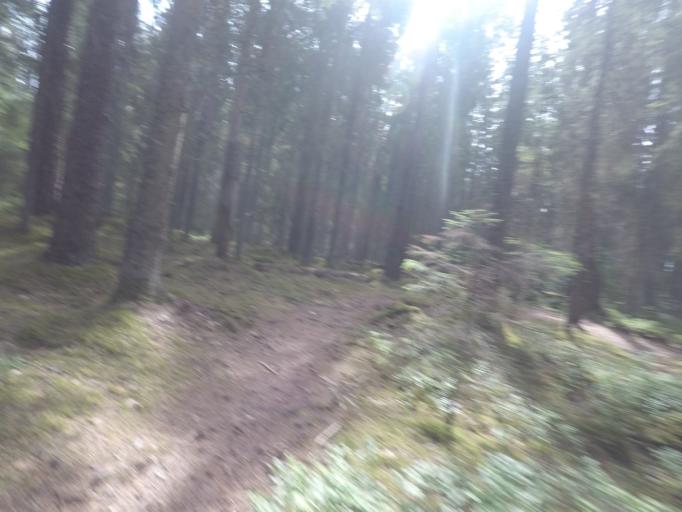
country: SE
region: Vaestmanland
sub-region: Kungsors Kommun
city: Kungsoer
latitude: 59.3639
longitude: 16.1060
